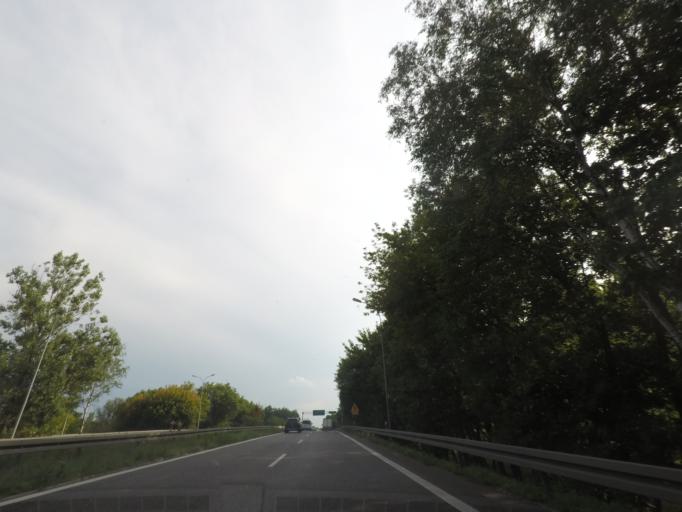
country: PL
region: Silesian Voivodeship
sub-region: Dabrowa Gornicza
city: Dabrowa Gornicza
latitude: 50.3195
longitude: 19.2378
